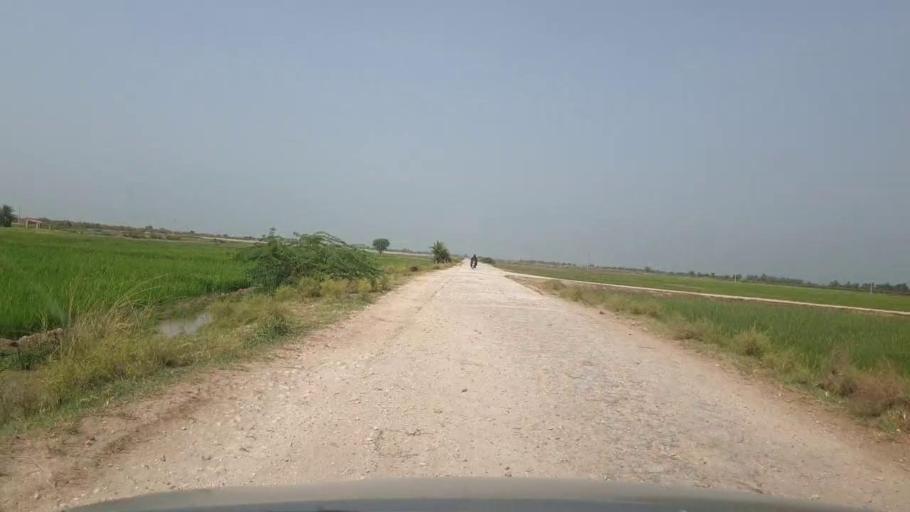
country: PK
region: Sindh
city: Garhi Yasin
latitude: 27.9156
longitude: 68.4231
